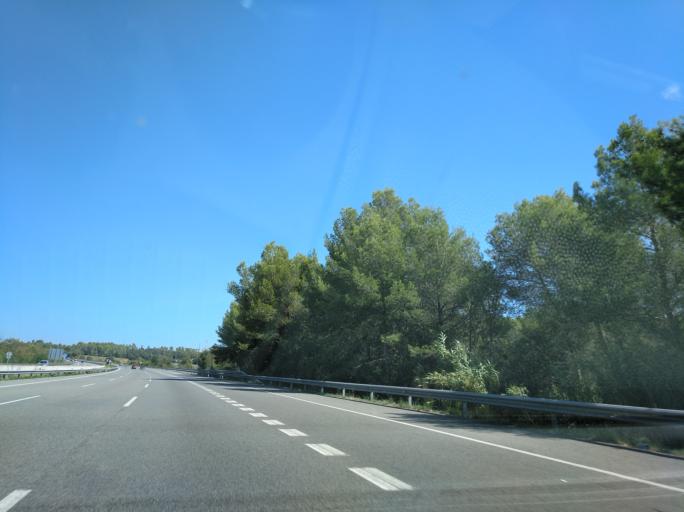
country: ES
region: Catalonia
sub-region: Provincia de Girona
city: Pontos
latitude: 42.1759
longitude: 2.9324
